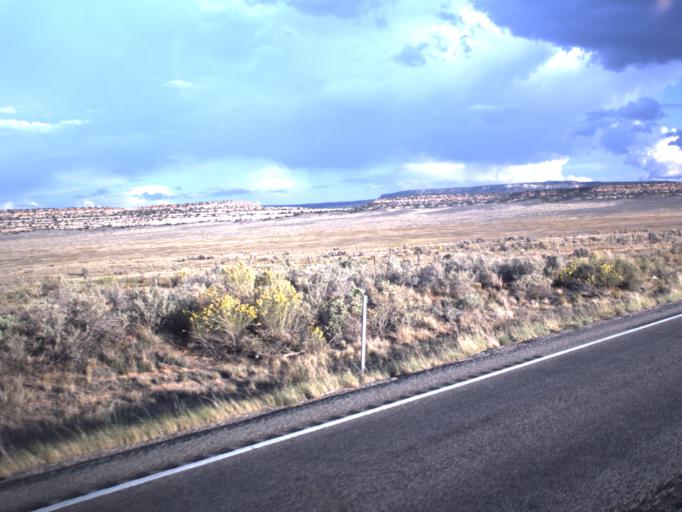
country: US
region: Utah
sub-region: San Juan County
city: Monticello
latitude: 38.1224
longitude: -109.3671
